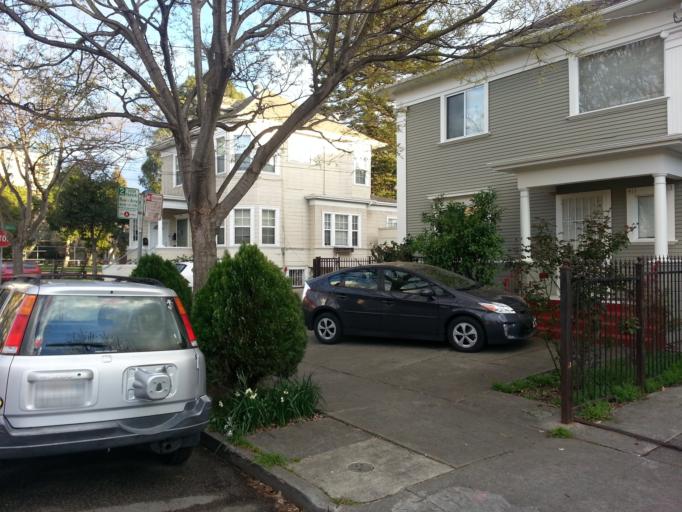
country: US
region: California
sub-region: Alameda County
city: Oakland
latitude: 37.8247
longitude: -122.2624
